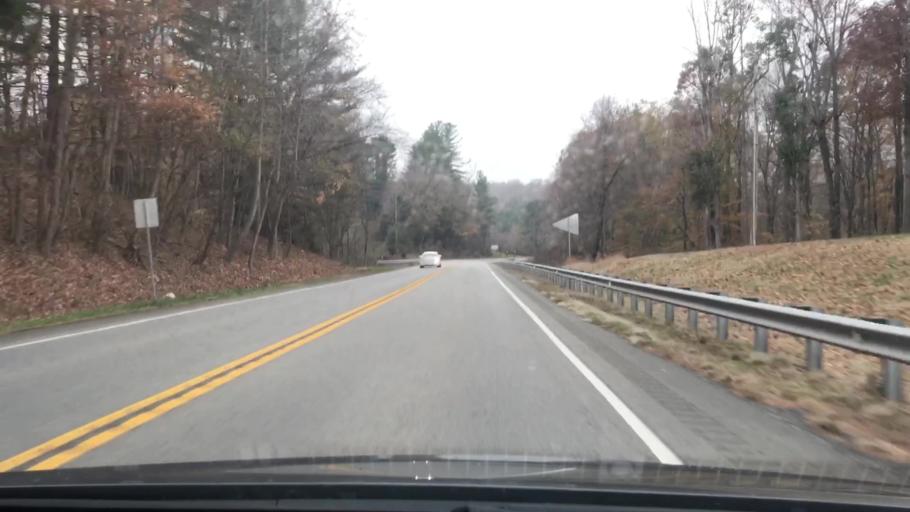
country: US
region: Kentucky
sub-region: Allen County
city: Scottsville
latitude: 36.8374
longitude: -86.0844
